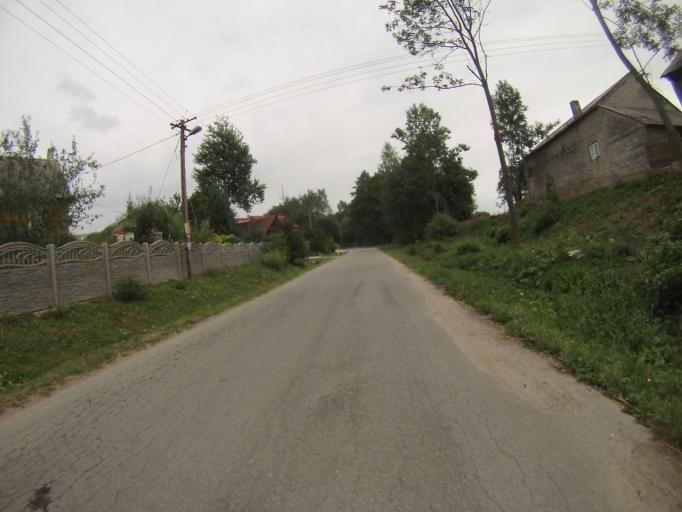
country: PL
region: Swietokrzyskie
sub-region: Powiat kielecki
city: Lagow
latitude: 50.7359
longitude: 21.0460
